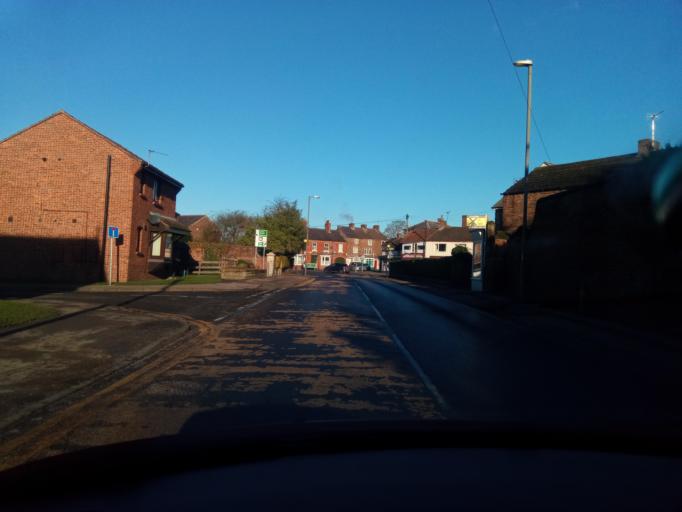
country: GB
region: England
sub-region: North Yorkshire
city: Thirsk
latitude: 54.2300
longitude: -1.3460
